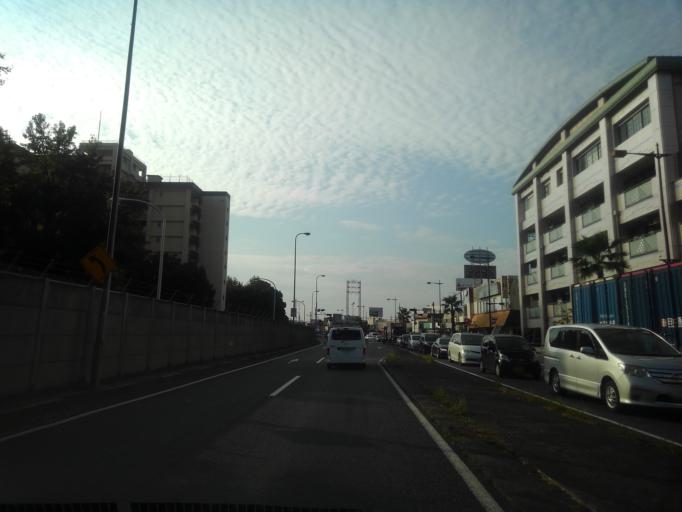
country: JP
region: Tokyo
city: Fussa
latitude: 35.7408
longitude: 139.3381
